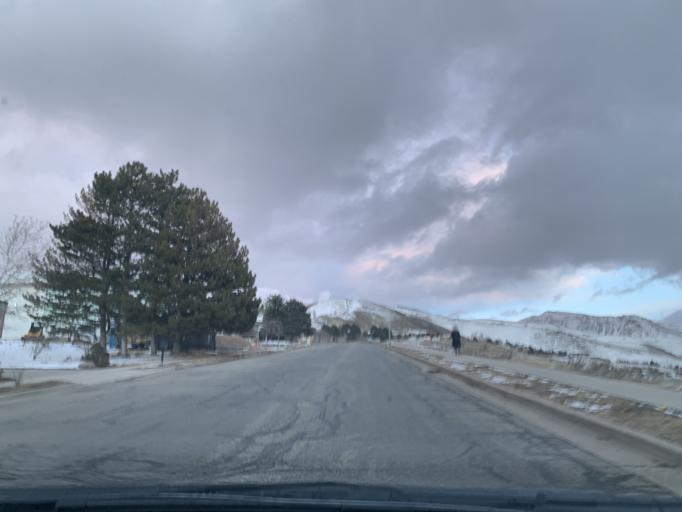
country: US
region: Utah
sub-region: Salt Lake County
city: Salt Lake City
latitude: 40.7792
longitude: -111.8499
